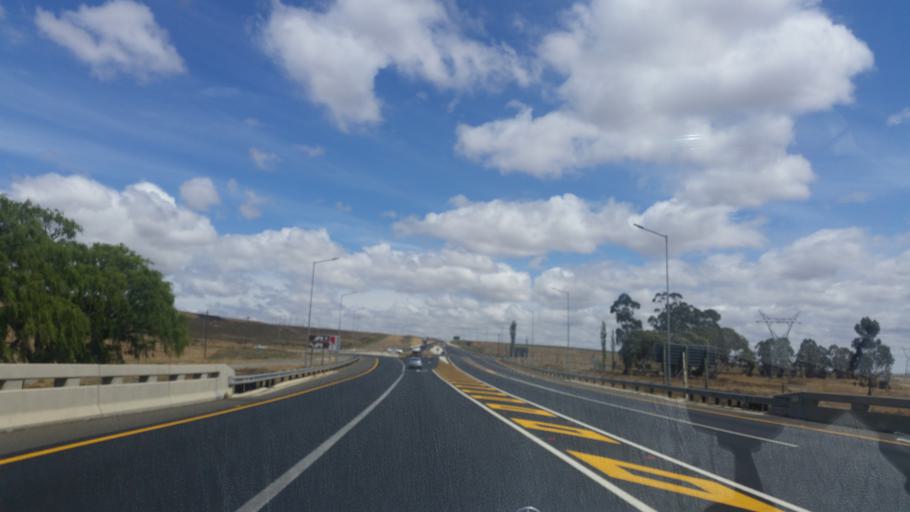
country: ZA
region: Orange Free State
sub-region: Thabo Mofutsanyana District Municipality
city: Harrismith
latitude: -28.2888
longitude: 29.0909
